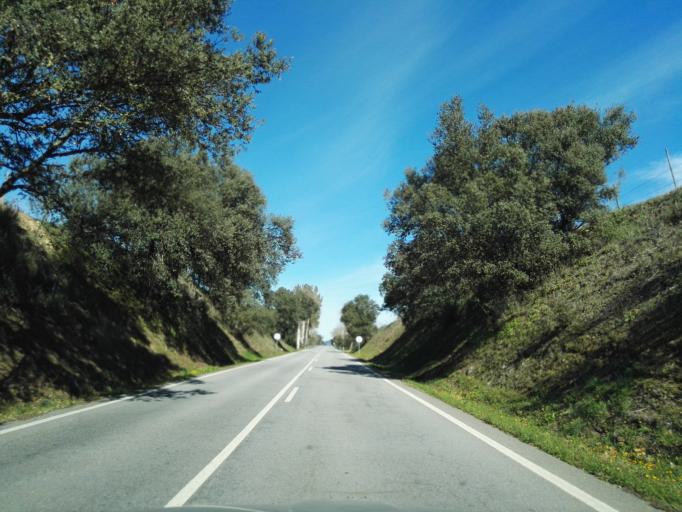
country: PT
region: Portalegre
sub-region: Arronches
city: Arronches
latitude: 39.0948
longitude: -7.2818
